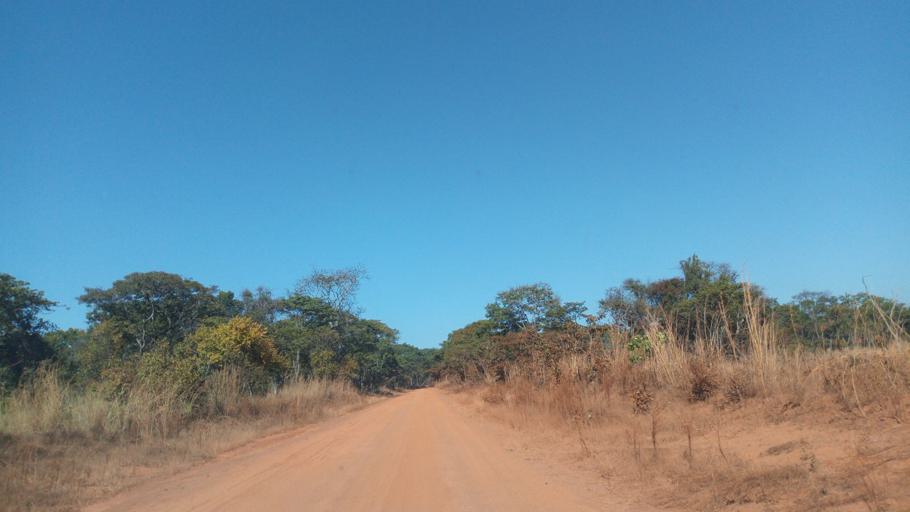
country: ZM
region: Luapula
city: Mwense
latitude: -10.6931
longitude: 28.3879
